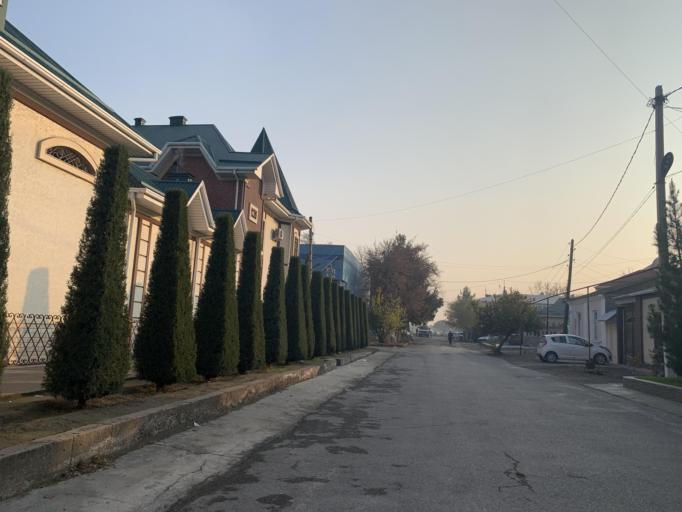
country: UZ
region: Fergana
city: Qo`qon
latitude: 40.5211
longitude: 70.9381
